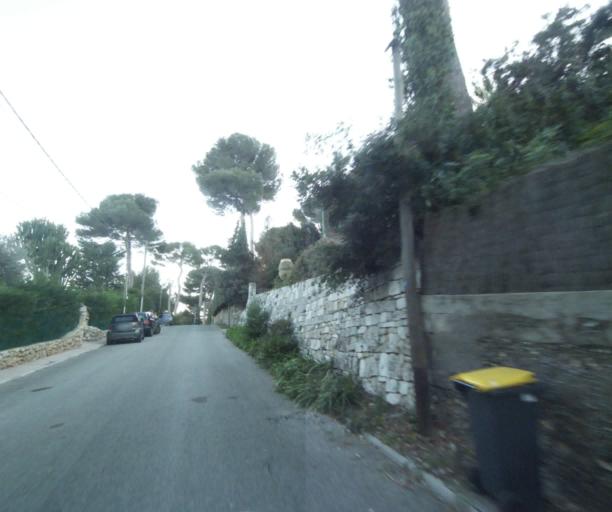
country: FR
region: Provence-Alpes-Cote d'Azur
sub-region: Departement des Alpes-Maritimes
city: Antibes
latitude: 43.5662
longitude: 7.1345
